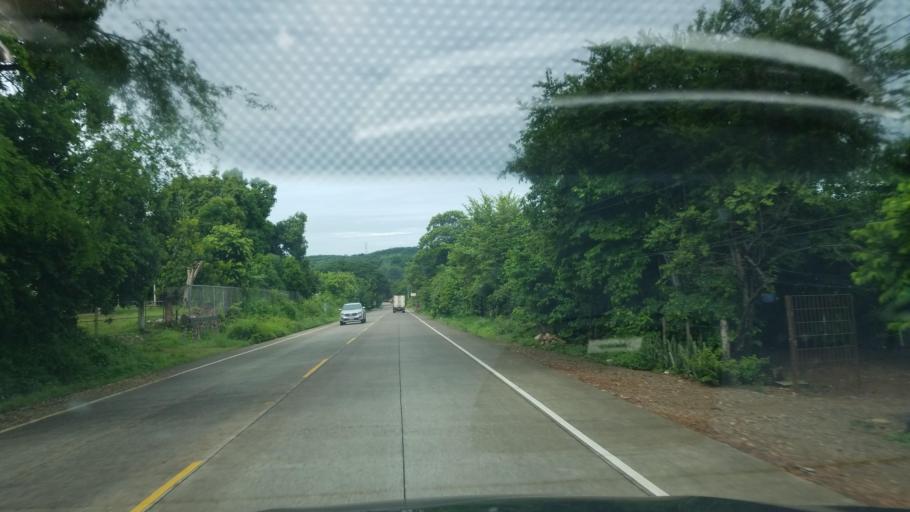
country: HN
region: Choluteca
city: Pespire
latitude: 13.6298
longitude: -87.3709
